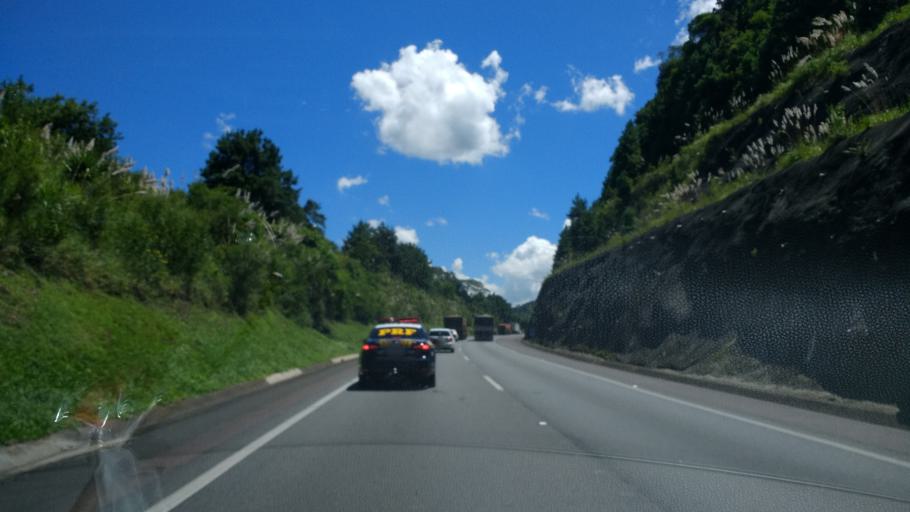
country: BR
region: Parana
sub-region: Campo Largo
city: Campo Largo
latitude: -25.4554
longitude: -49.6284
